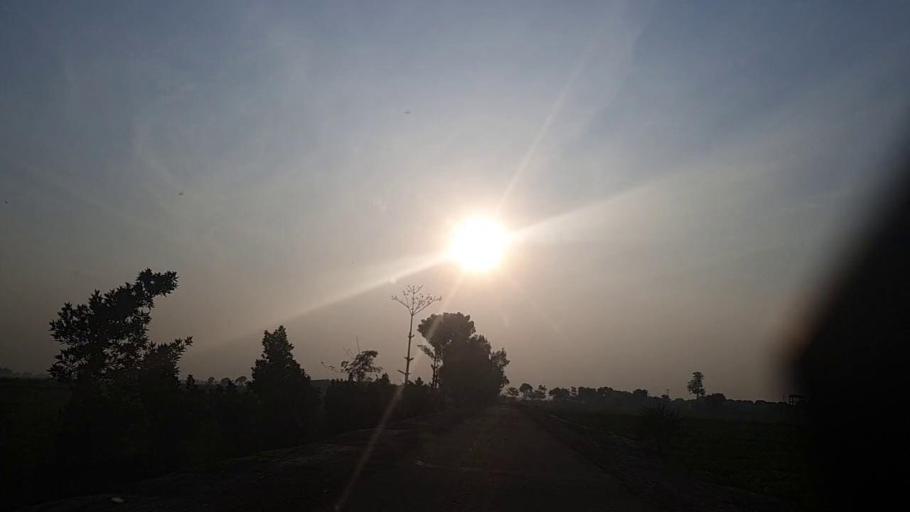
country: PK
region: Sindh
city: Sakrand
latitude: 26.1222
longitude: 68.2285
